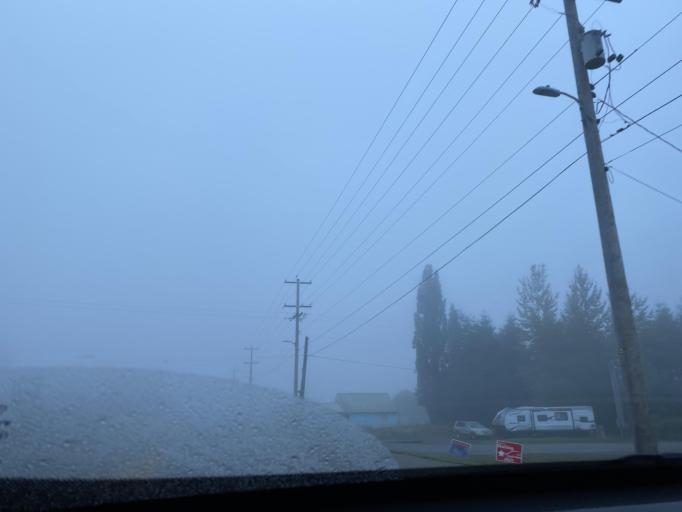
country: US
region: Washington
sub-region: Clallam County
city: Forks
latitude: 47.9445
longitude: -124.3855
